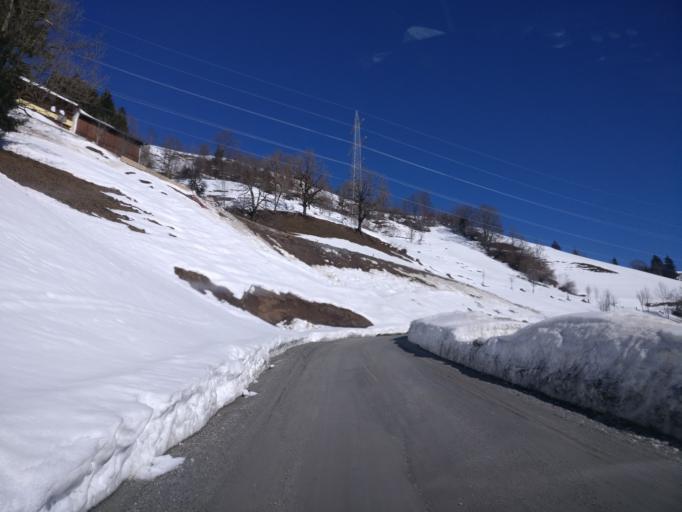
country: AT
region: Salzburg
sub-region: Politischer Bezirk Sankt Johann im Pongau
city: Sankt Johann im Pongau
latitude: 47.3355
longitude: 13.2361
